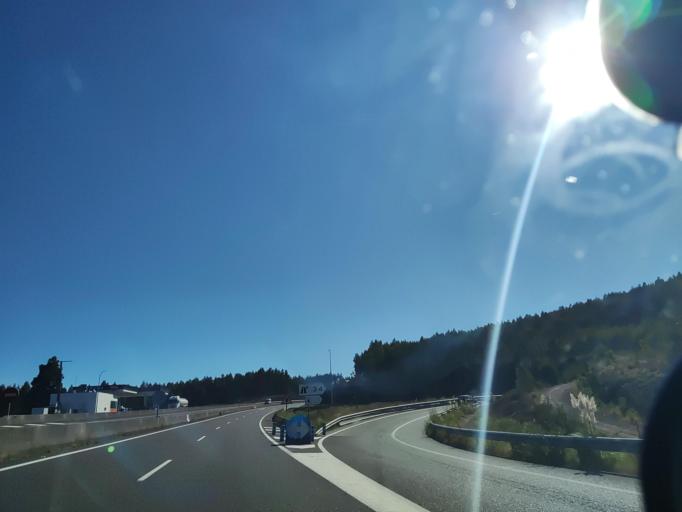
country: ES
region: Galicia
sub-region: Provincia da Coruna
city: Boiro
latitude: 42.6097
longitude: -8.9631
